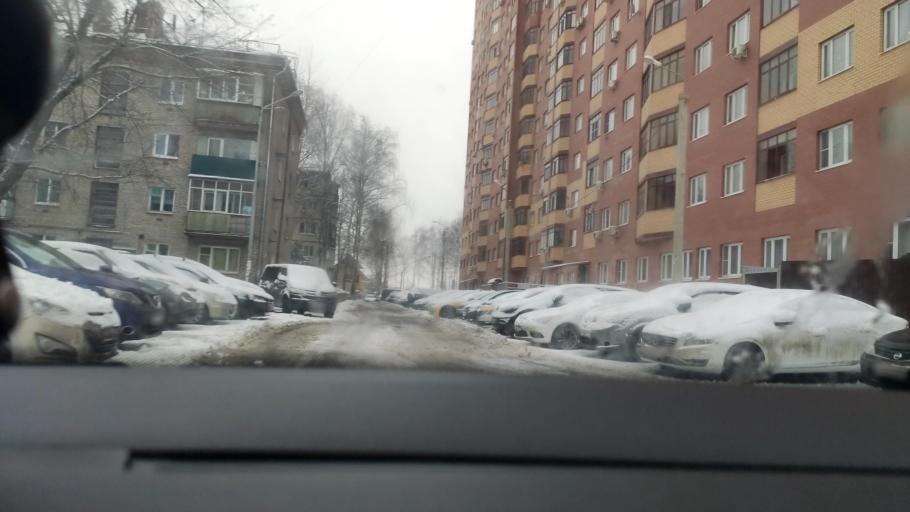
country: RU
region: Moscow
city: Strogino
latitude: 55.8637
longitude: 37.3928
